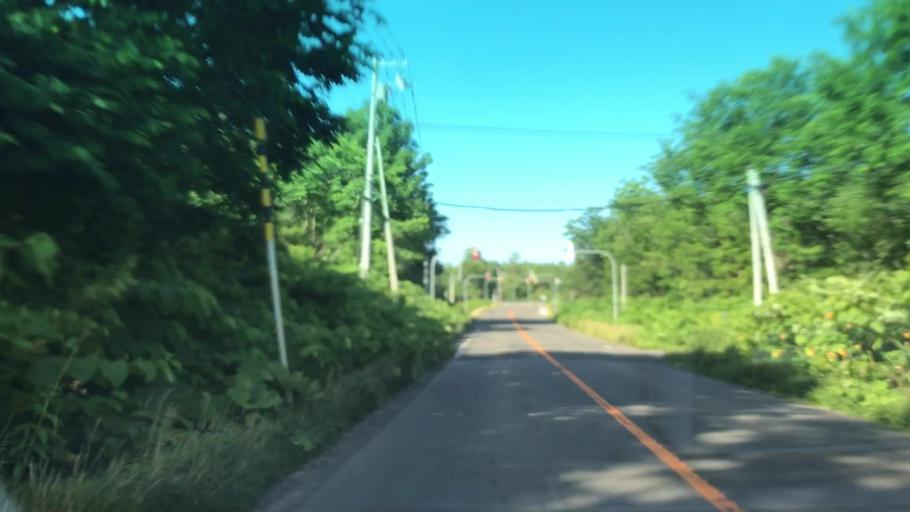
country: JP
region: Hokkaido
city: Yoichi
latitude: 43.0596
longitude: 140.8688
